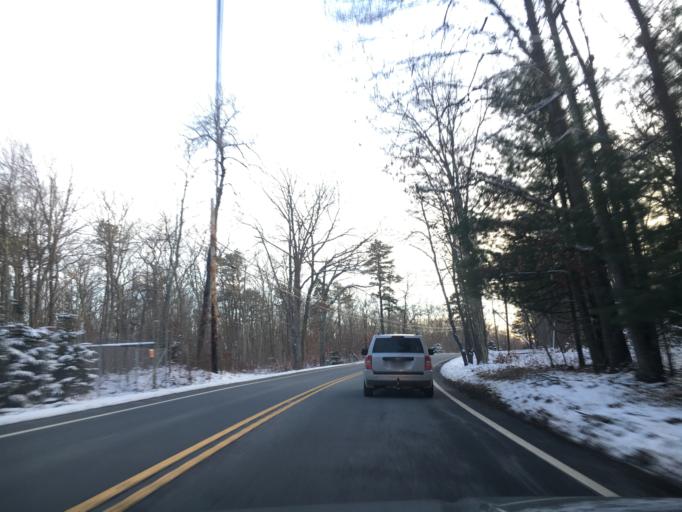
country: US
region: Pennsylvania
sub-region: Pike County
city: Hemlock Farms
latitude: 41.2448
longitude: -75.0679
